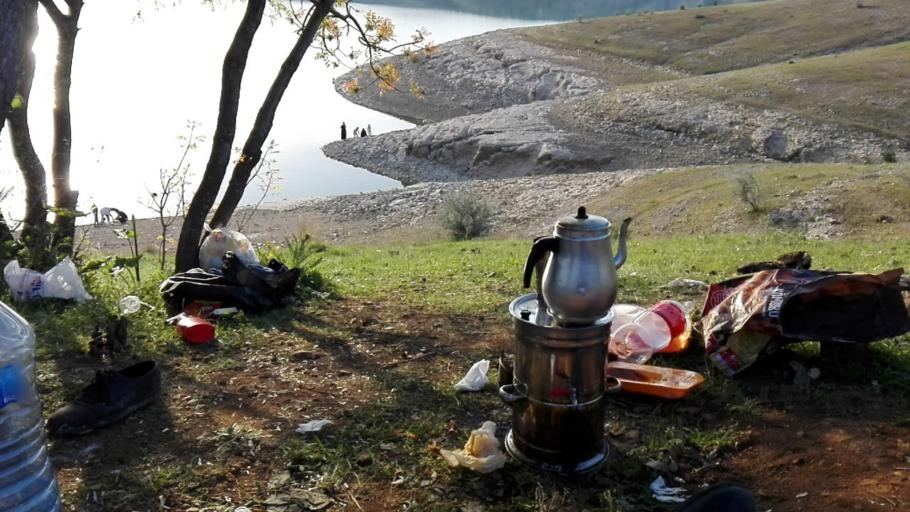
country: TR
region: Diyarbakir
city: Malabadi
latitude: 38.1770
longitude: 41.2181
